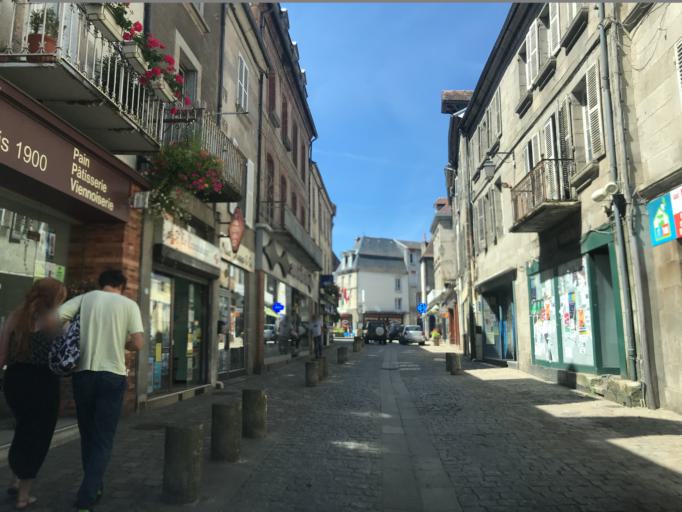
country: FR
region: Limousin
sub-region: Departement de la Creuse
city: Felletin
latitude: 45.8831
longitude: 2.1739
